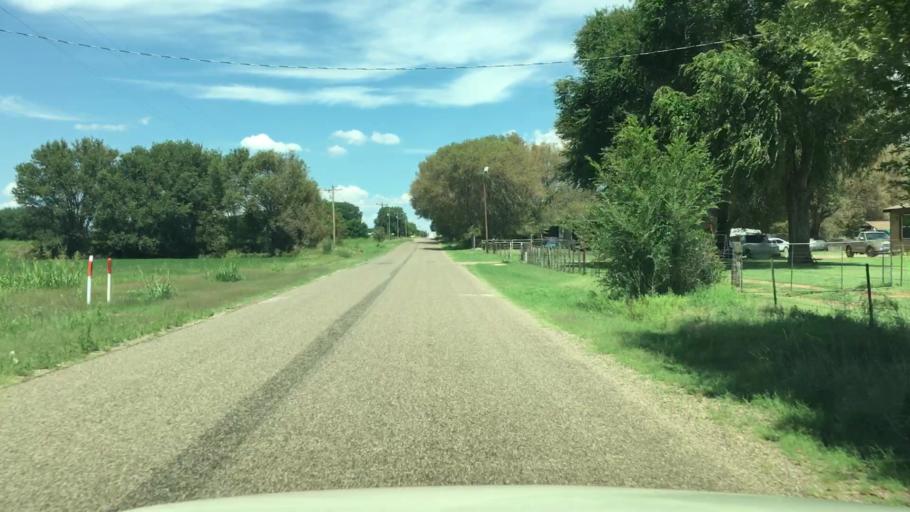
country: US
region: New Mexico
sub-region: De Baca County
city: Fort Sumner
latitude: 34.4367
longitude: -104.1936
